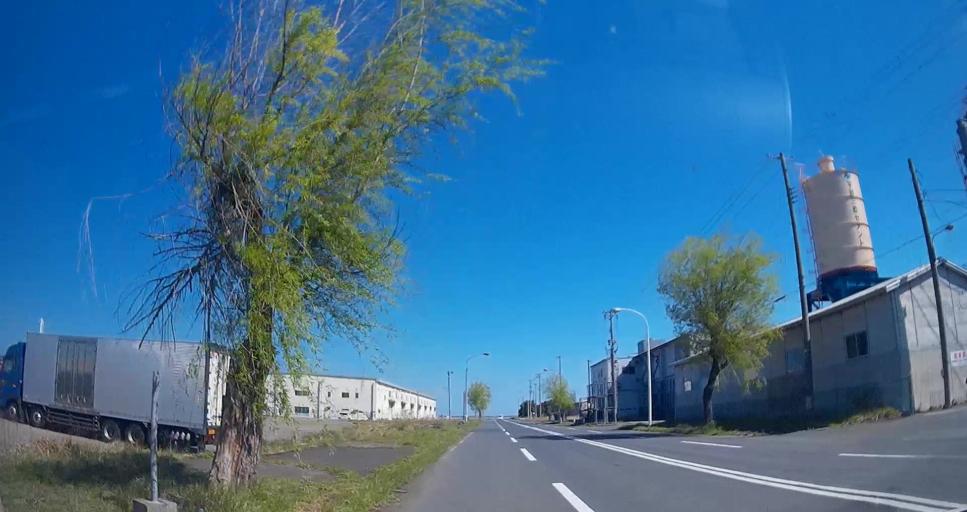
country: JP
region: Aomori
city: Hachinohe
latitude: 40.5280
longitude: 141.5448
